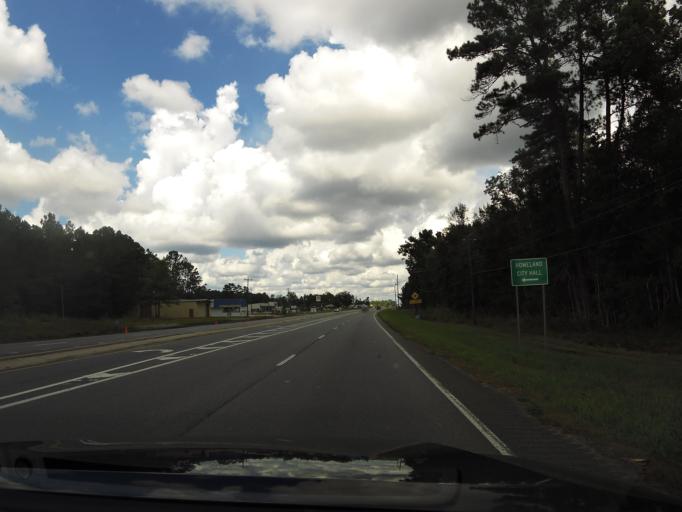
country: US
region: Georgia
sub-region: Charlton County
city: Folkston
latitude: 30.8536
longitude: -82.0098
